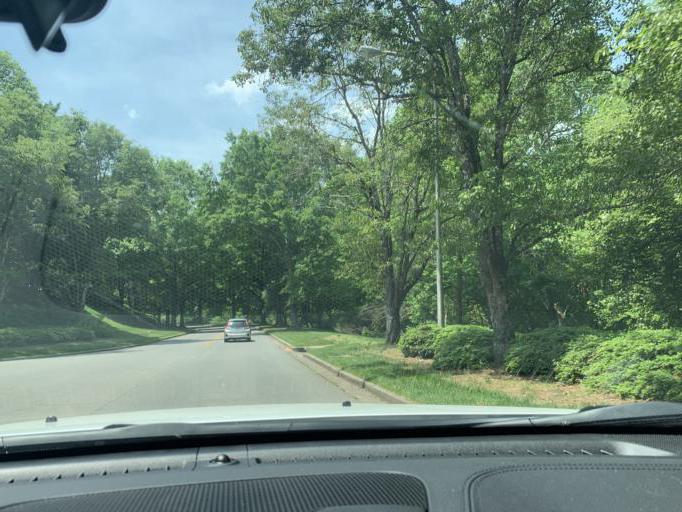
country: US
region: Georgia
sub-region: Fulton County
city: Johns Creek
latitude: 34.1107
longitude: -84.1996
